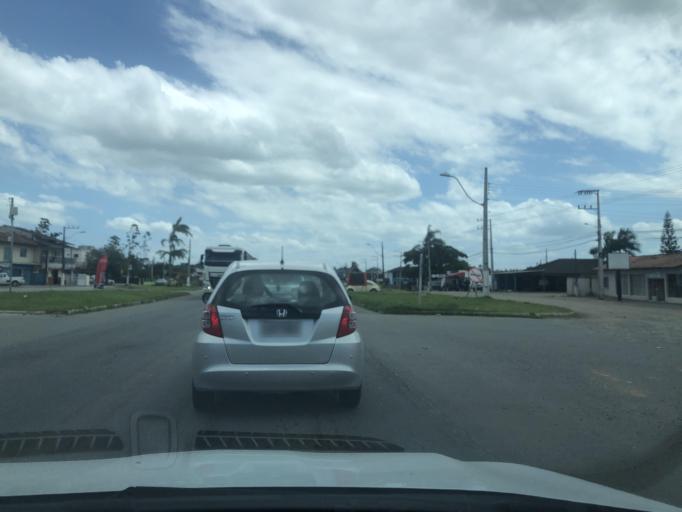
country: BR
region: Santa Catarina
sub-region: Joinville
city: Joinville
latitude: -26.3992
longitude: -48.7417
